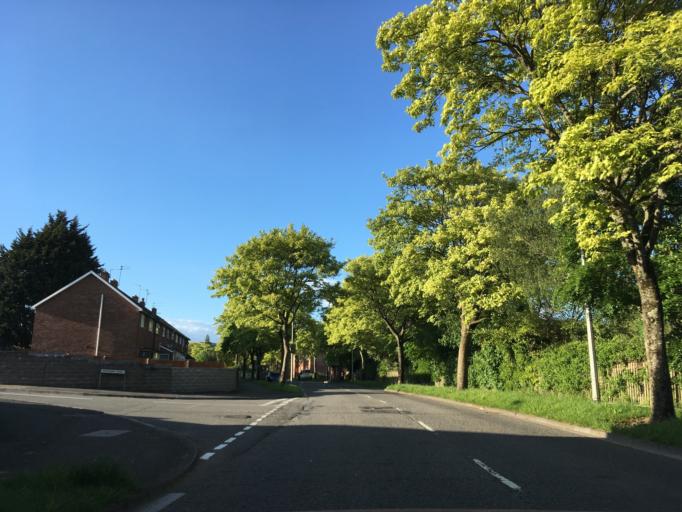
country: GB
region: Wales
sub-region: Newport
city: Marshfield
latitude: 51.5059
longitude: -3.1204
